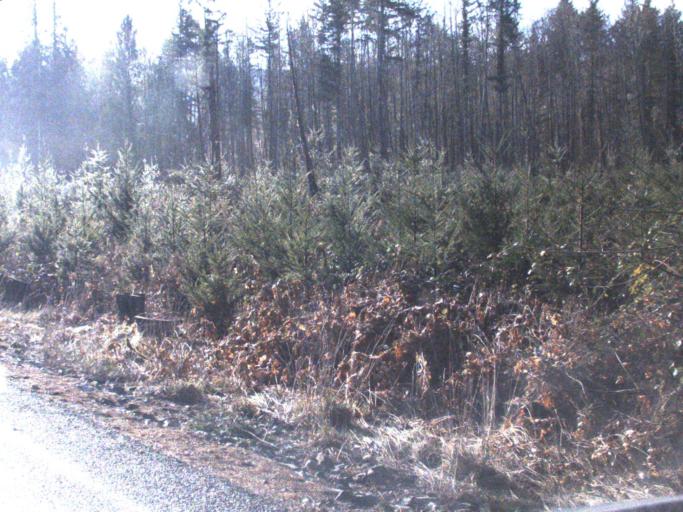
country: US
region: Washington
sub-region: Snohomish County
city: Darrington
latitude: 48.4785
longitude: -121.5912
